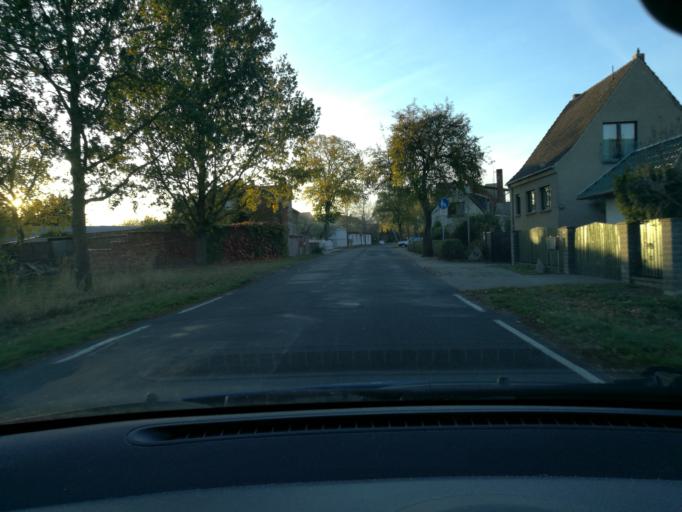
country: DE
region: Brandenburg
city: Perleberg
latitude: 53.0790
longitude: 11.8074
